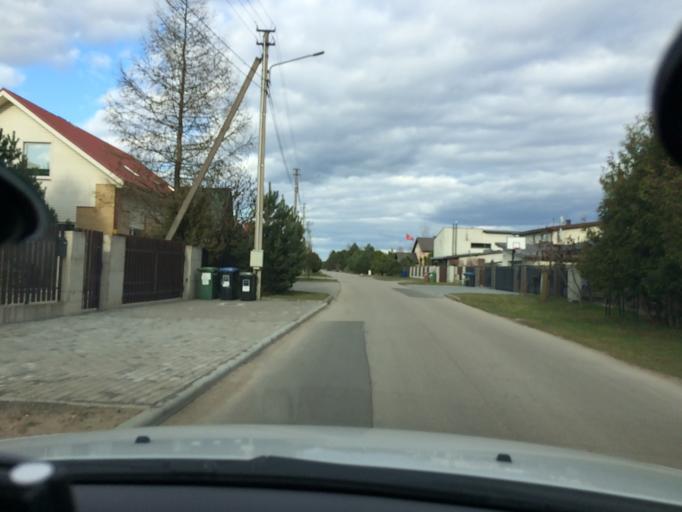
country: LT
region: Vilnius County
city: Rasos
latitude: 54.7749
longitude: 25.3511
